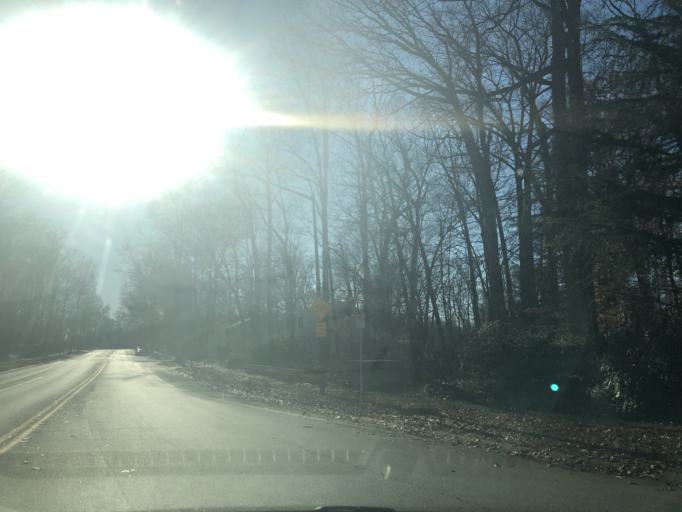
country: US
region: Maryland
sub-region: Howard County
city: Columbia
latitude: 39.2058
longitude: -76.8469
